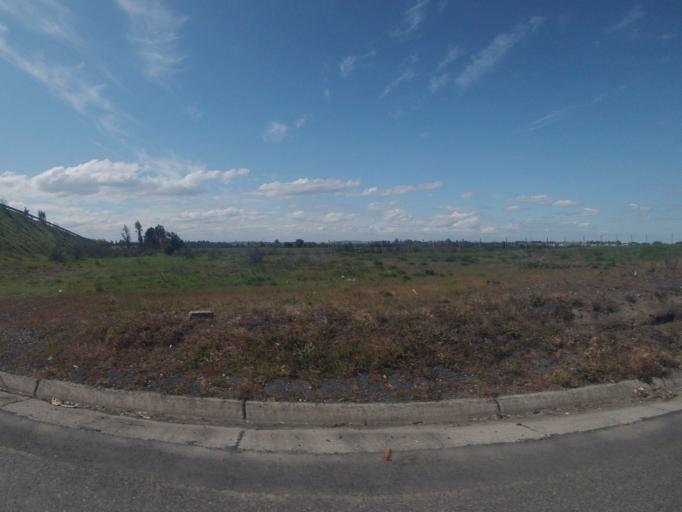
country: CL
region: Biobio
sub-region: Provincia de Biobio
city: Los Angeles
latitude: -37.4524
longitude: -72.4085
